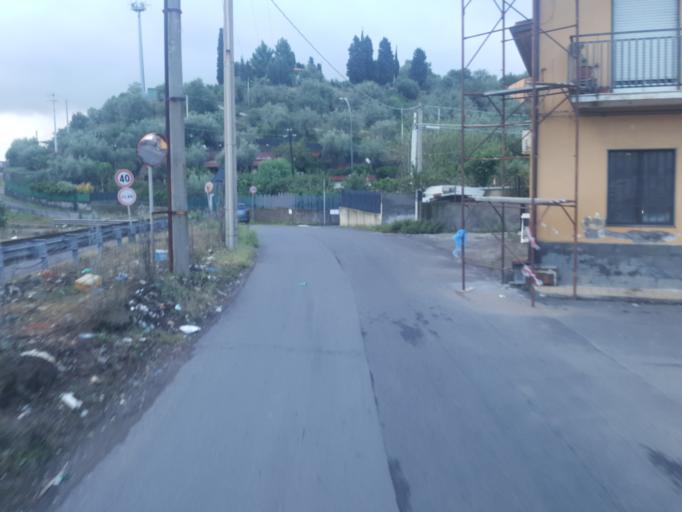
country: IT
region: Sicily
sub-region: Catania
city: Belvedere-Piano Tavola
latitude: 37.5347
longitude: 14.9833
